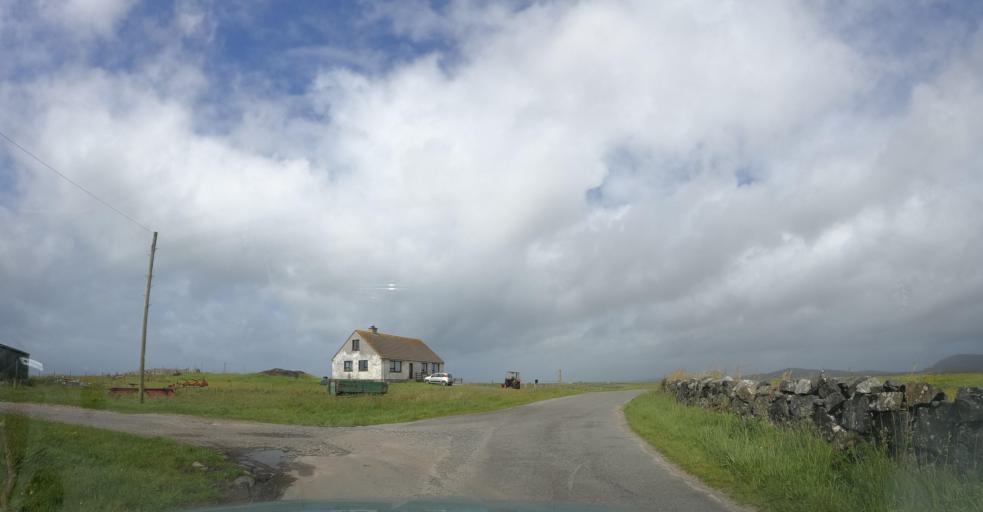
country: GB
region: Scotland
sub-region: Eilean Siar
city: Isle of South Uist
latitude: 57.2612
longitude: -7.4079
